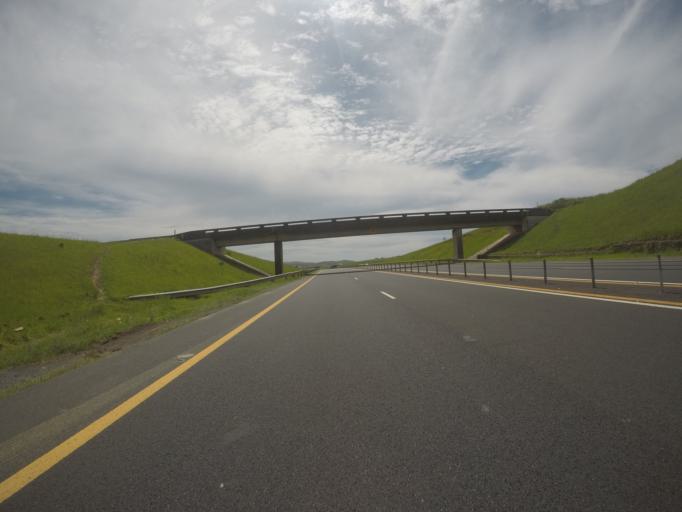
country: ZA
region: KwaZulu-Natal
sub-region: iLembe District Municipality
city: Mandeni
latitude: -29.1767
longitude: 31.5069
